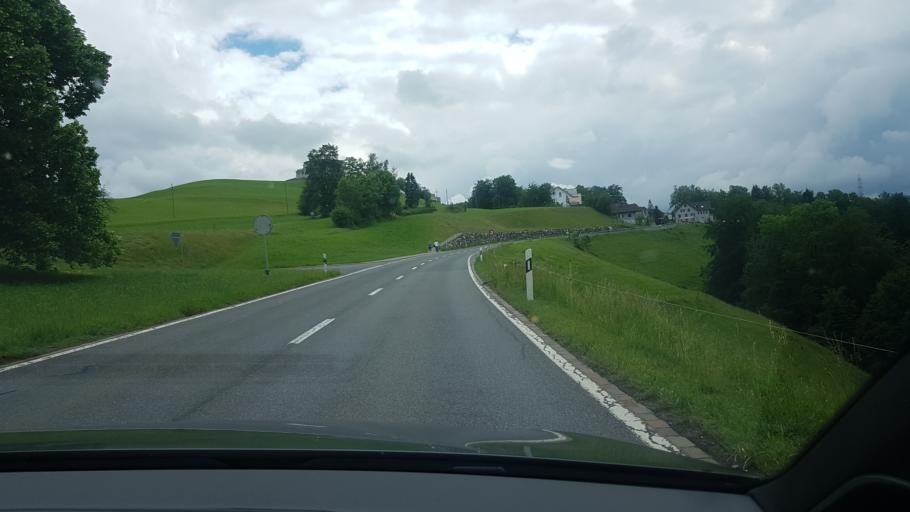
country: CH
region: Zug
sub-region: Zug
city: Menzingen
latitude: 47.1861
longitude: 8.5699
